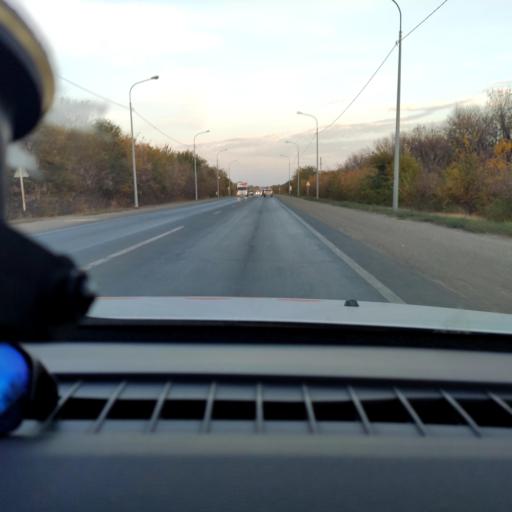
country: RU
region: Samara
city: Samara
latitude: 53.0808
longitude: 50.0946
